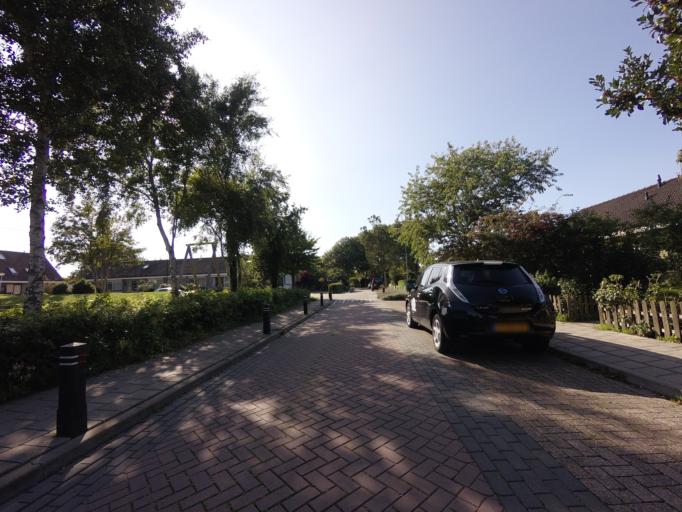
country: NL
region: Friesland
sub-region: Gemeente Terschelling
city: West-Terschelling
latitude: 53.3840
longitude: 5.2834
